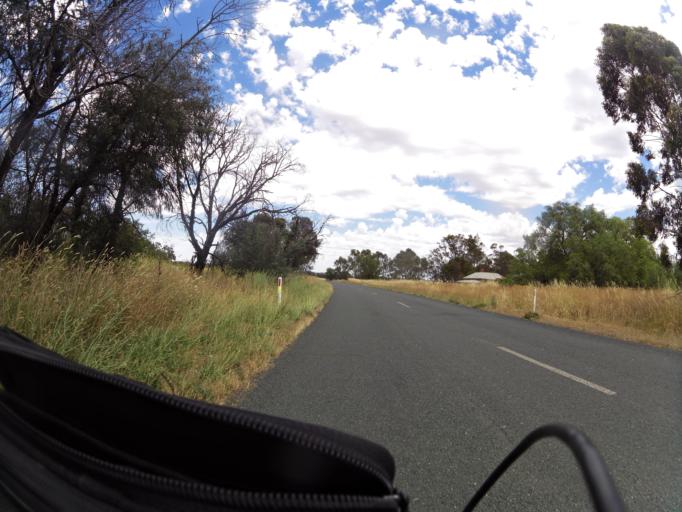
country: AU
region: Victoria
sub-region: Greater Shepparton
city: Shepparton
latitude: -36.6692
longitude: 145.1971
